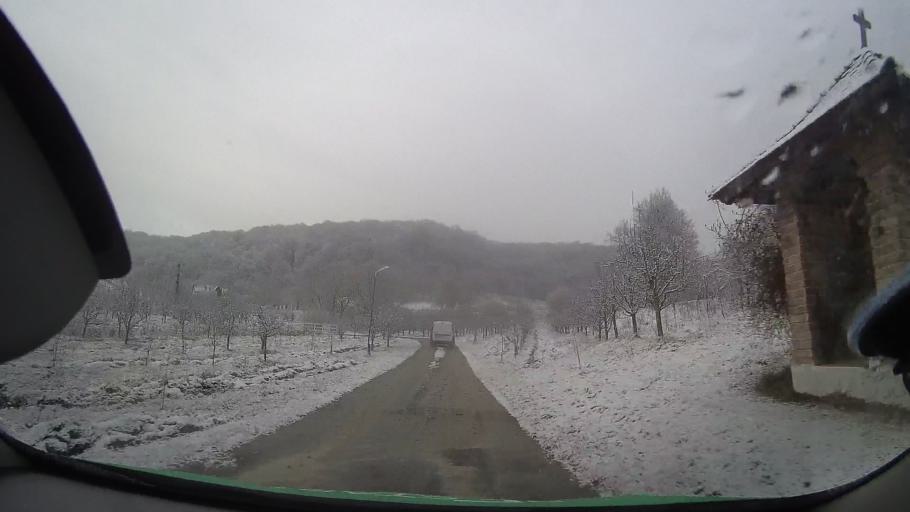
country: RO
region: Sibiu
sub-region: Municipiul Medias
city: Medias
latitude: 46.1586
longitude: 24.3796
